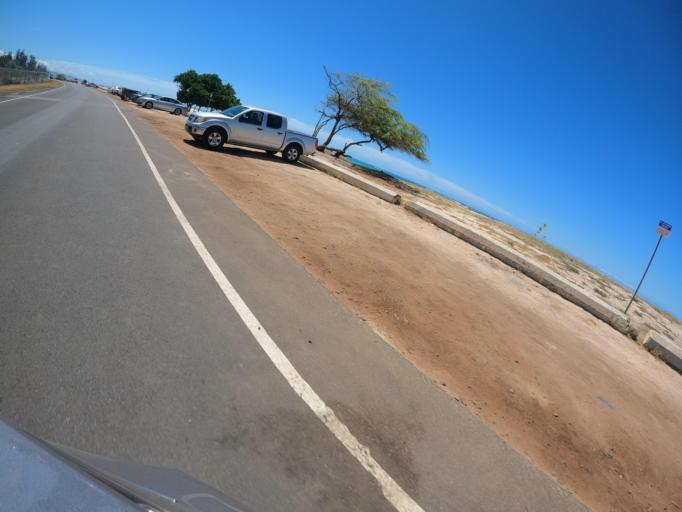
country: US
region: Hawaii
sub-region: Honolulu County
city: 'Ewa Villages
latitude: 21.3003
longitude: -158.0642
